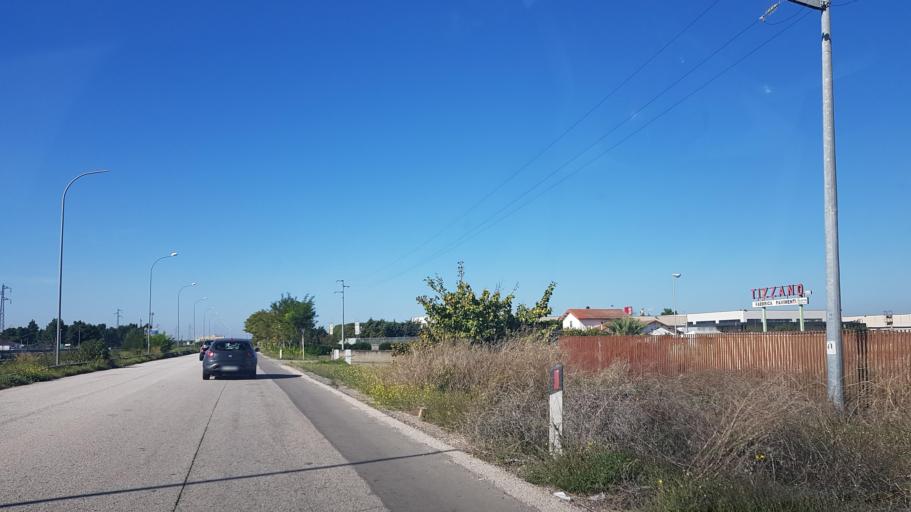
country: IT
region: Apulia
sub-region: Provincia di Foggia
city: Carapelle
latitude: 41.4127
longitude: 15.6300
